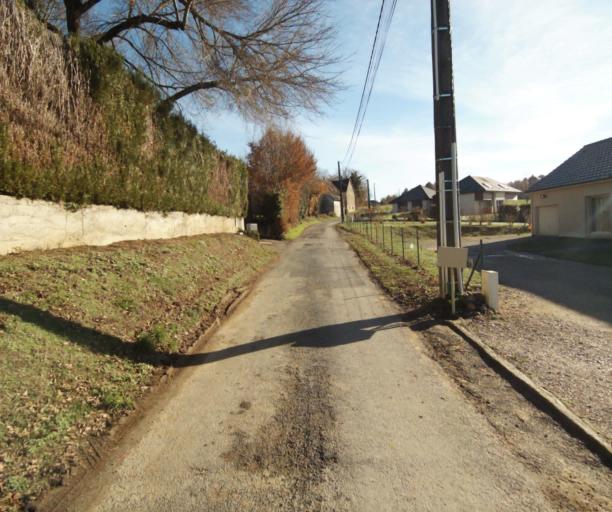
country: FR
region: Limousin
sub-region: Departement de la Correze
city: Laguenne
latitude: 45.2387
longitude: 1.7548
